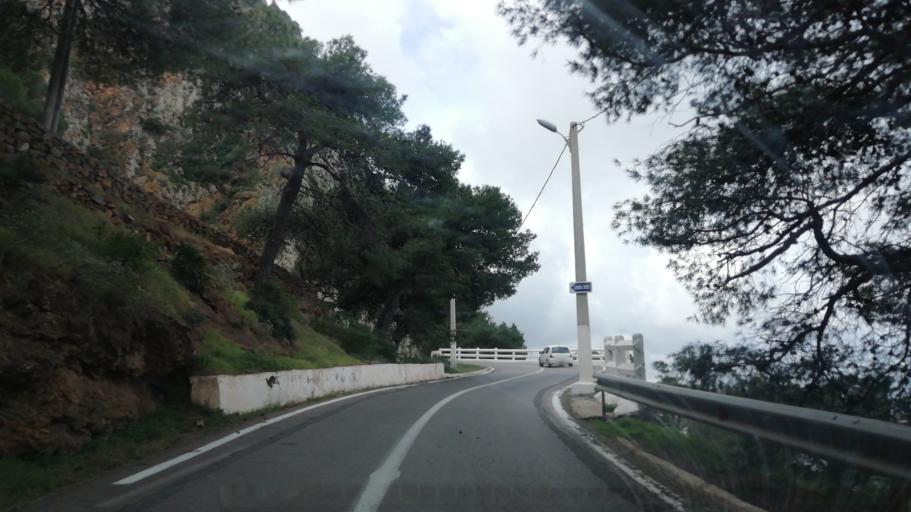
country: DZ
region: Oran
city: Oran
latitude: 35.7093
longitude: -0.6691
